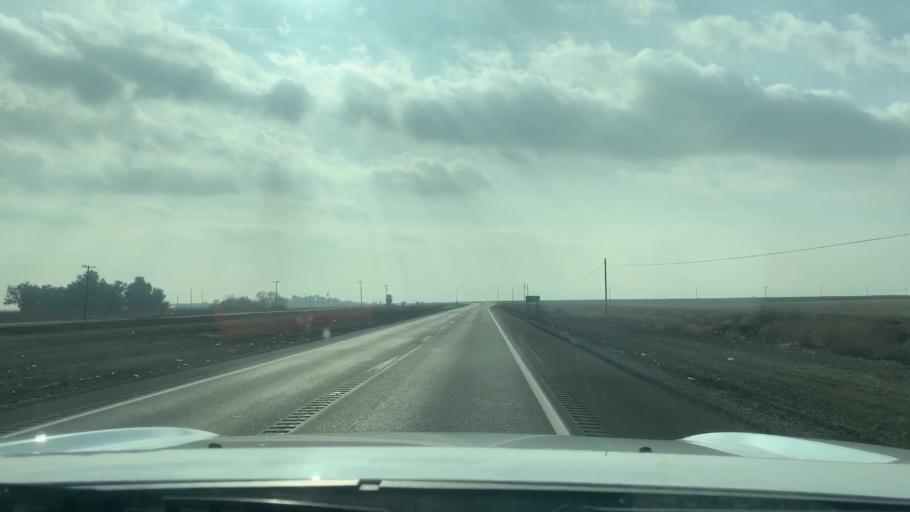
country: US
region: California
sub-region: Kings County
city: Stratford
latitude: 36.1405
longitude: -119.8757
